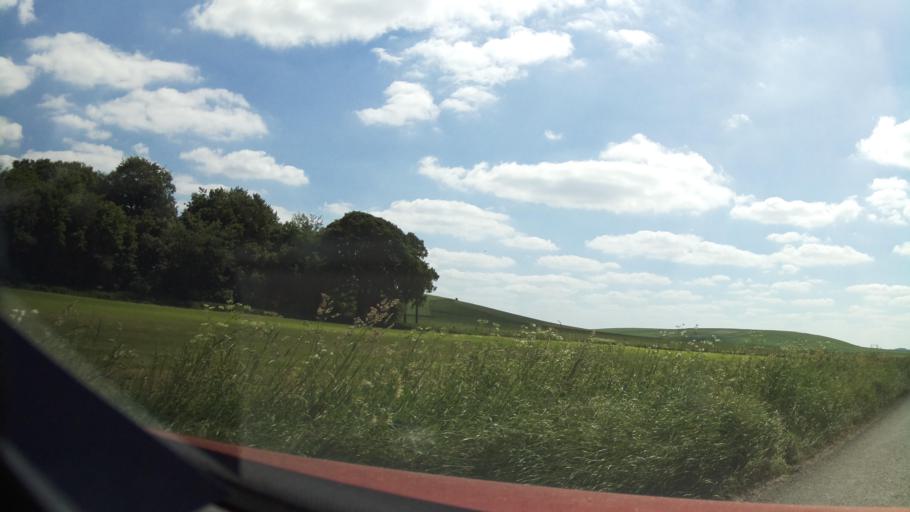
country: GB
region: England
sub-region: Wiltshire
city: Avebury
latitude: 51.4113
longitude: -1.9004
